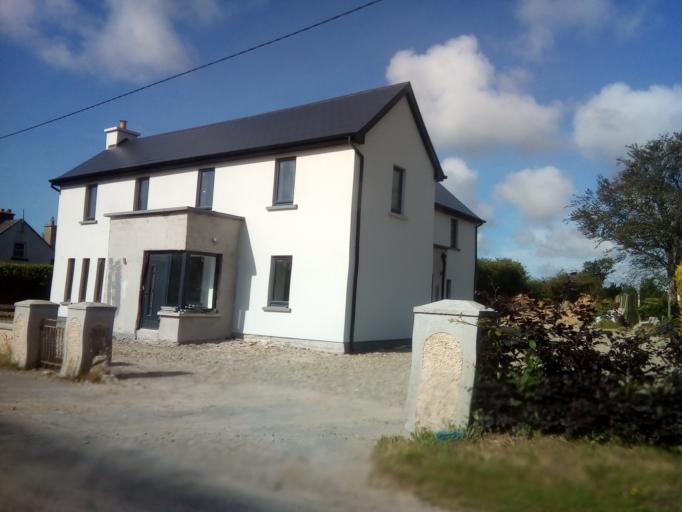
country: IE
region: Leinster
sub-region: Loch Garman
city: Loch Garman
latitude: 52.2439
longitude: -6.5504
